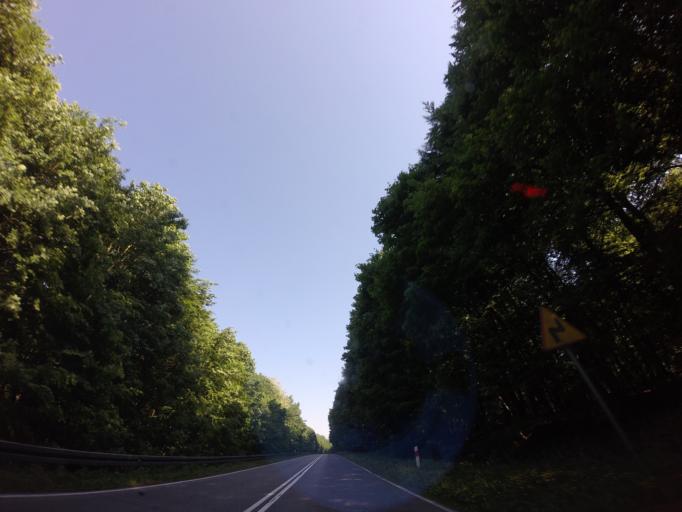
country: PL
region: West Pomeranian Voivodeship
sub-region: Powiat gryfinski
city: Stare Czarnowo
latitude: 53.3315
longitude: 14.7770
